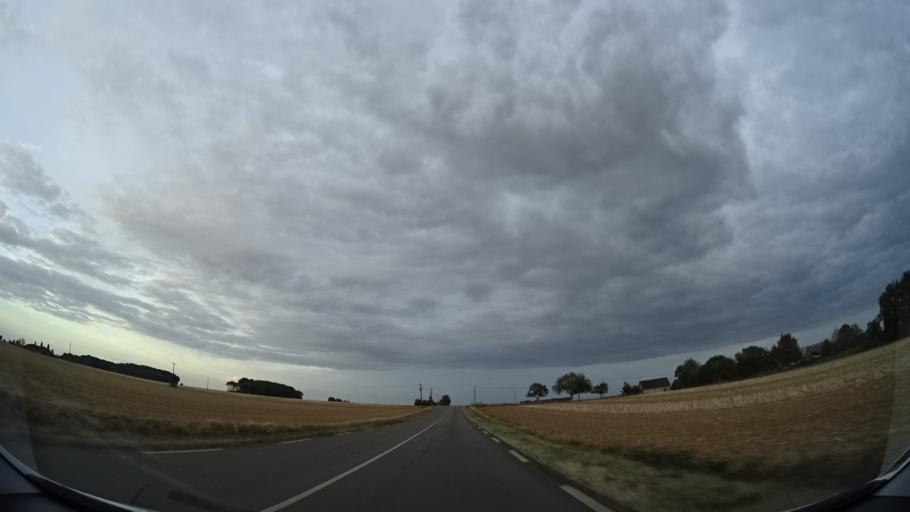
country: FR
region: Bourgogne
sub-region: Departement de l'Yonne
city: Charny
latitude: 47.9328
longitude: 3.1669
